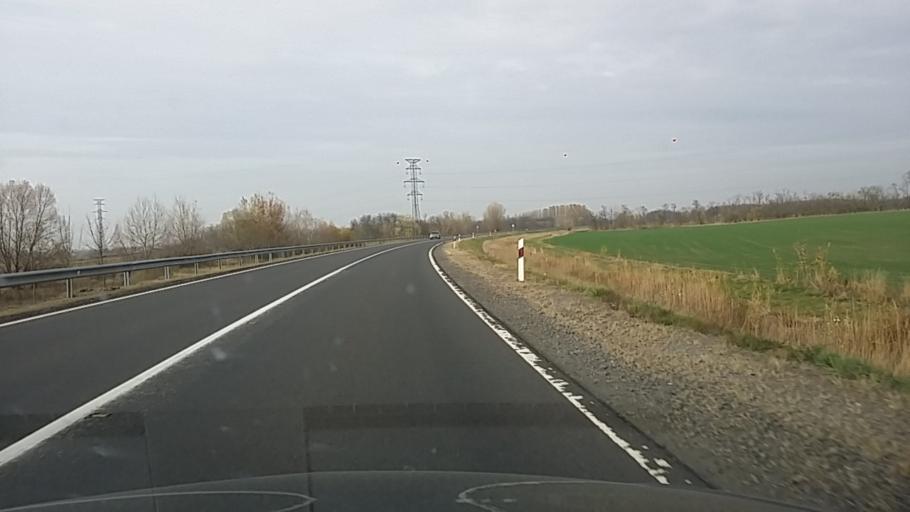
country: HU
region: Szabolcs-Szatmar-Bereg
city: Nyirpazony
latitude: 47.9611
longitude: 21.8159
